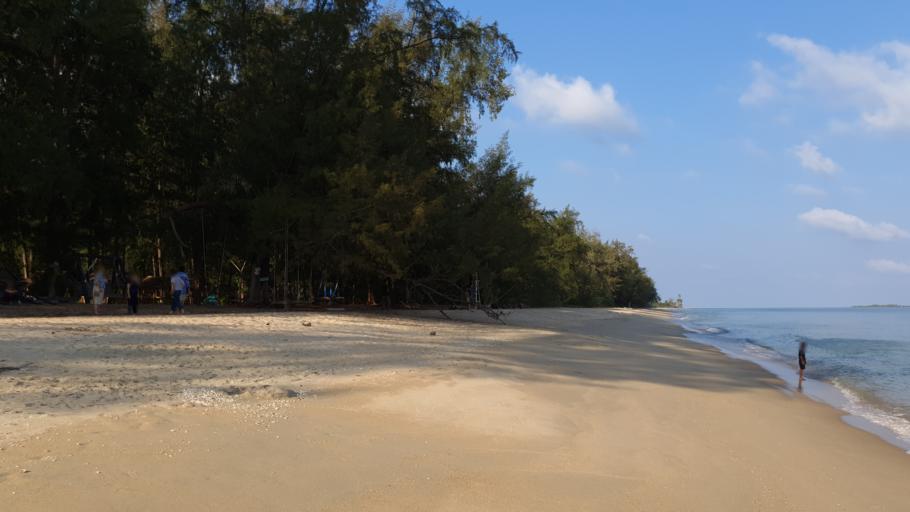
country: TH
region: Prachuap Khiri Khan
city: Thap Sakae
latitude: 11.3835
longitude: 99.5883
